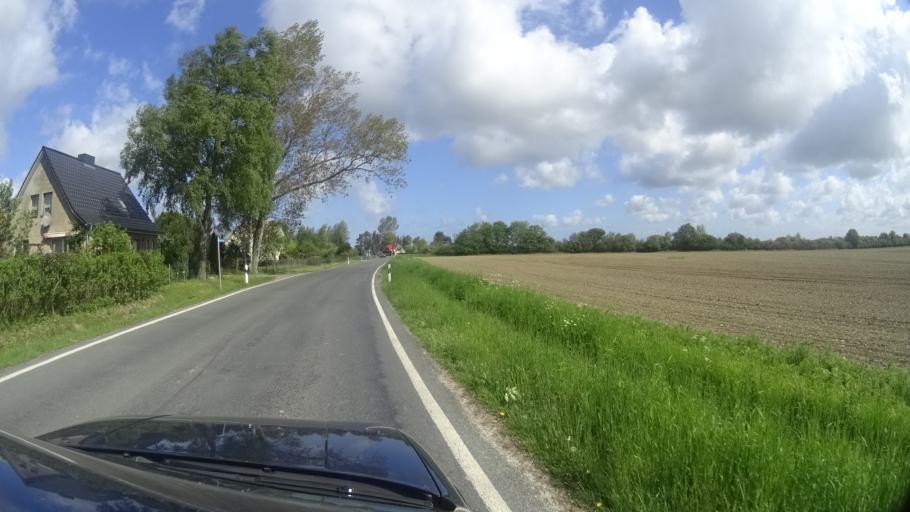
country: DE
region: Mecklenburg-Vorpommern
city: Trinwillershagen
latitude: 54.3123
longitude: 12.5853
